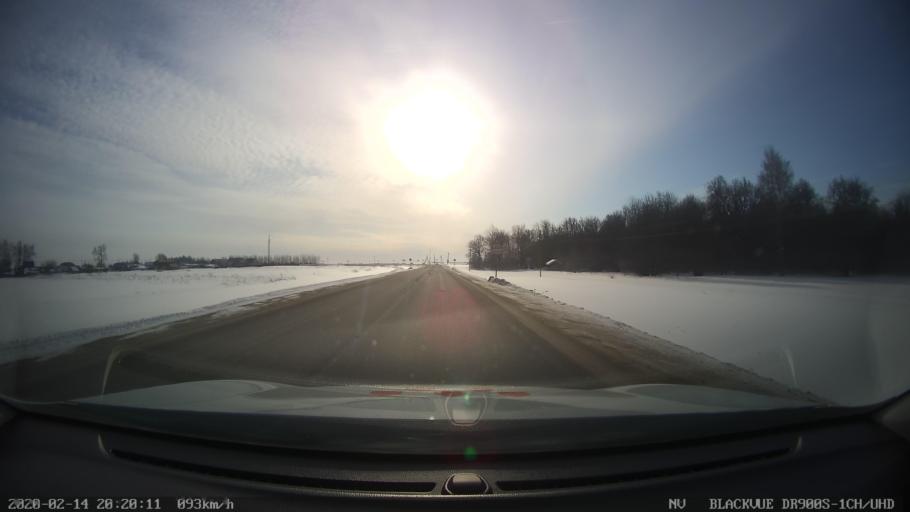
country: RU
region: Tatarstan
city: Verkhniy Uslon
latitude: 55.5597
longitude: 48.9024
